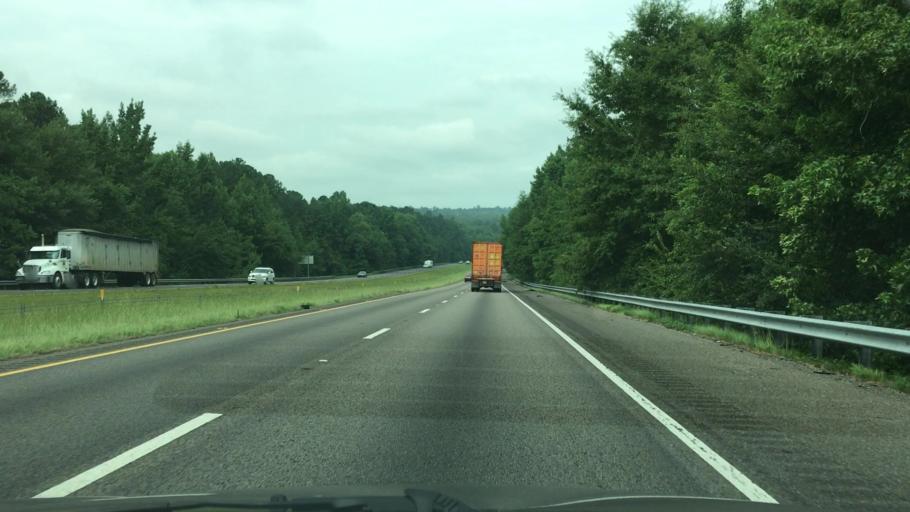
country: US
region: South Carolina
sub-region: Edgefield County
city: Murphys Estates
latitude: 33.5743
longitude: -81.9085
